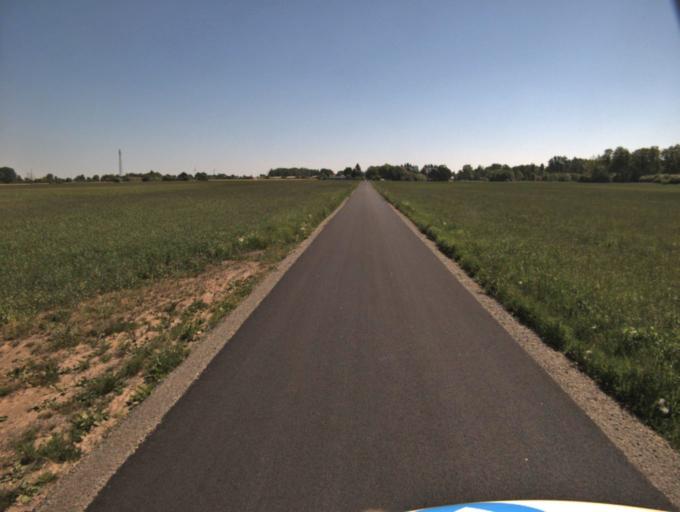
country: SE
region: Skane
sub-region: Kristianstads Kommun
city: Kristianstad
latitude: 56.0168
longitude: 14.2080
